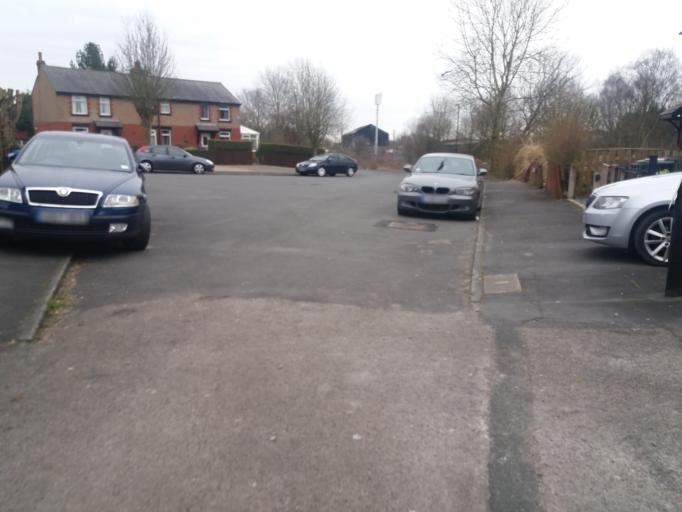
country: GB
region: England
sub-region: Lancashire
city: Chorley
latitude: 53.6644
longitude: -2.6276
